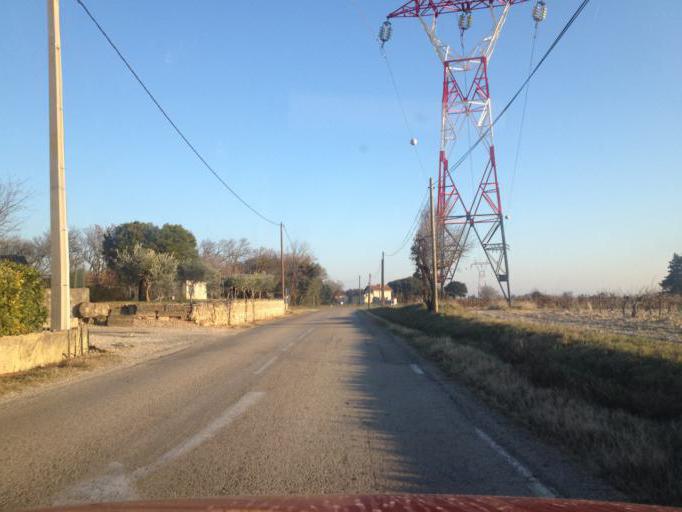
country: FR
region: Provence-Alpes-Cote d'Azur
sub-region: Departement du Vaucluse
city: Camaret-sur-Aigues
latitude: 44.1639
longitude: 4.8963
